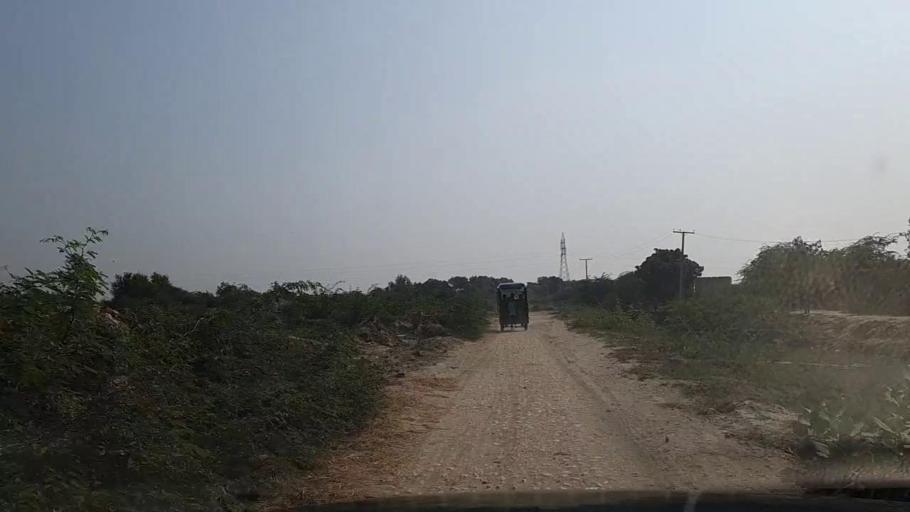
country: PK
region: Sindh
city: Mirpur Batoro
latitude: 24.7036
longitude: 68.2168
